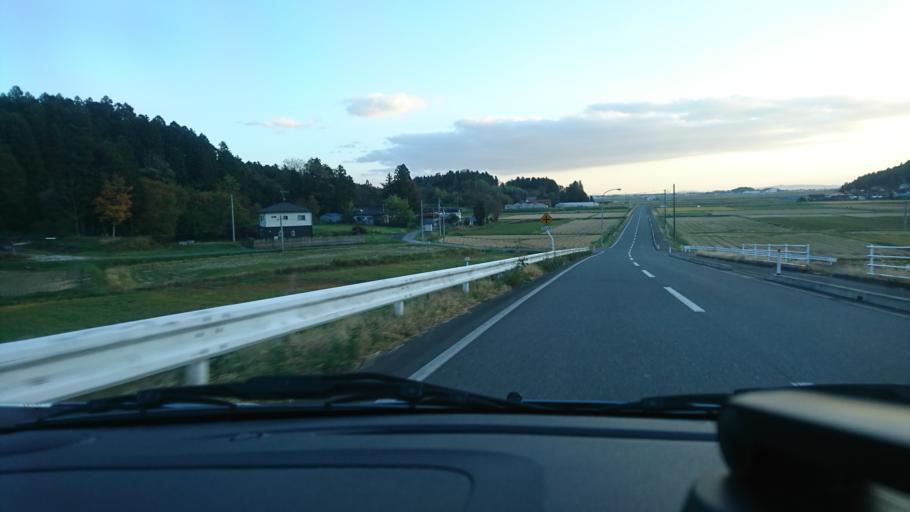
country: JP
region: Iwate
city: Ichinoseki
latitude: 38.7649
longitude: 141.2383
